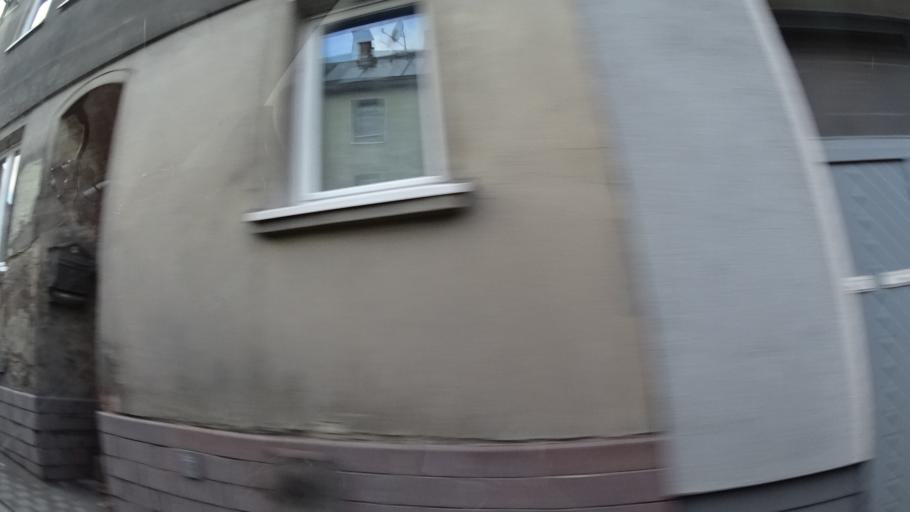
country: DE
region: Thuringia
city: Auma
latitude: 50.7007
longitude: 11.9003
